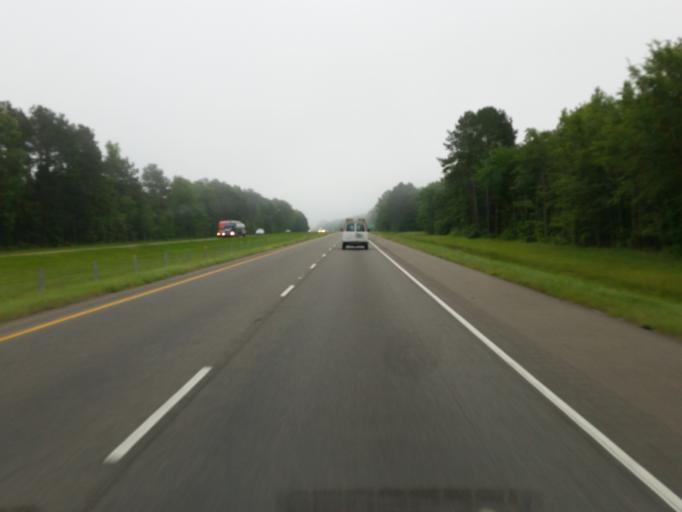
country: US
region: Louisiana
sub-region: Bossier Parish
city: Haughton
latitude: 32.5769
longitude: -93.4590
